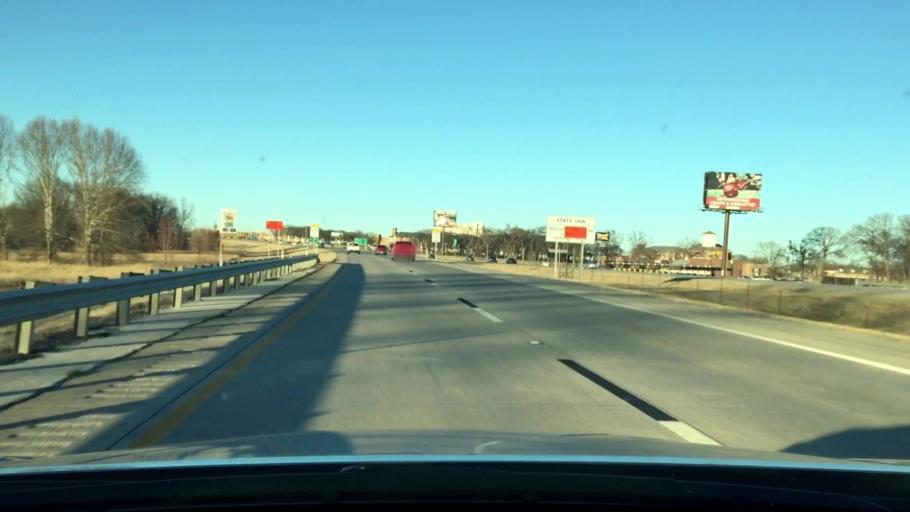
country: US
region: Texas
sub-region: Cooke County
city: Gainesville
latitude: 33.7467
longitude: -97.1374
